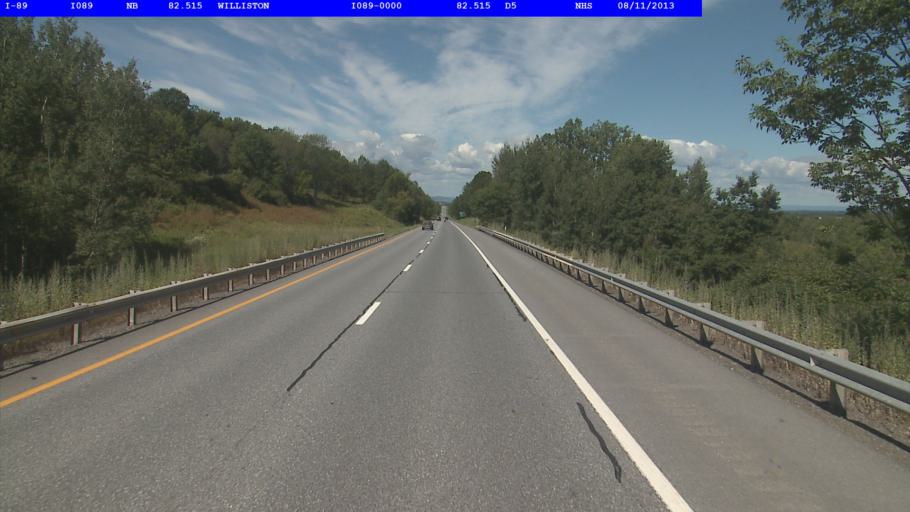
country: US
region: Vermont
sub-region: Chittenden County
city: Williston
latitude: 44.4368
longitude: -73.0861
